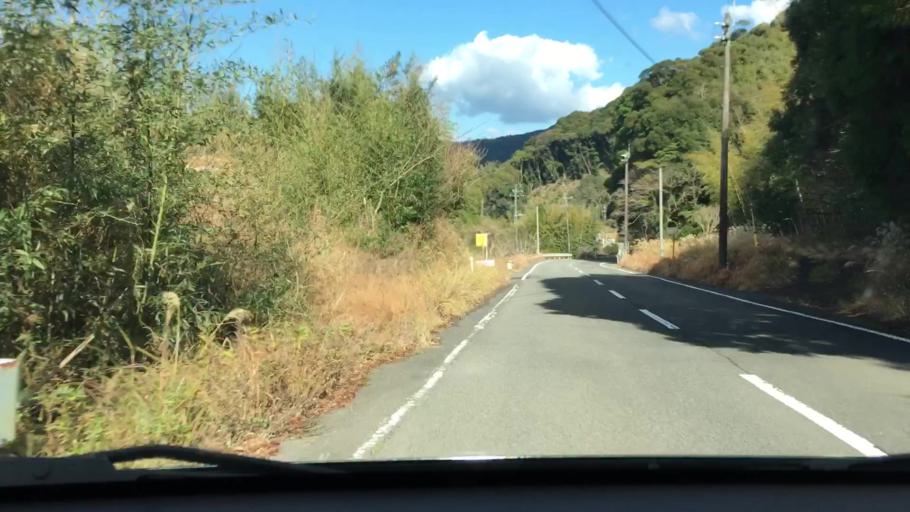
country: JP
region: Kagoshima
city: Ijuin
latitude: 31.7243
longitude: 130.4169
